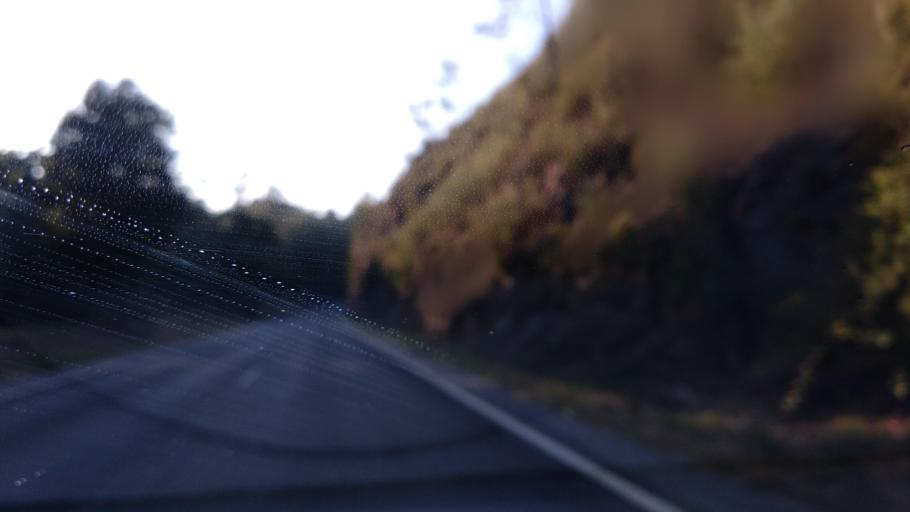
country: ES
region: Galicia
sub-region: Provincia de Pontevedra
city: Ponte Caldelas
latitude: 42.3392
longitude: -8.5543
